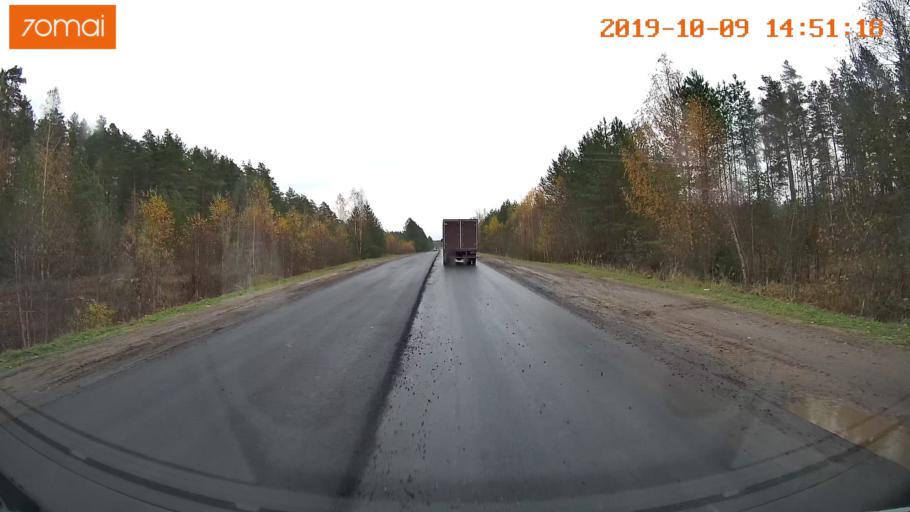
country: RU
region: Kostroma
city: Chistyye Bory
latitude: 58.3790
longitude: 41.6124
